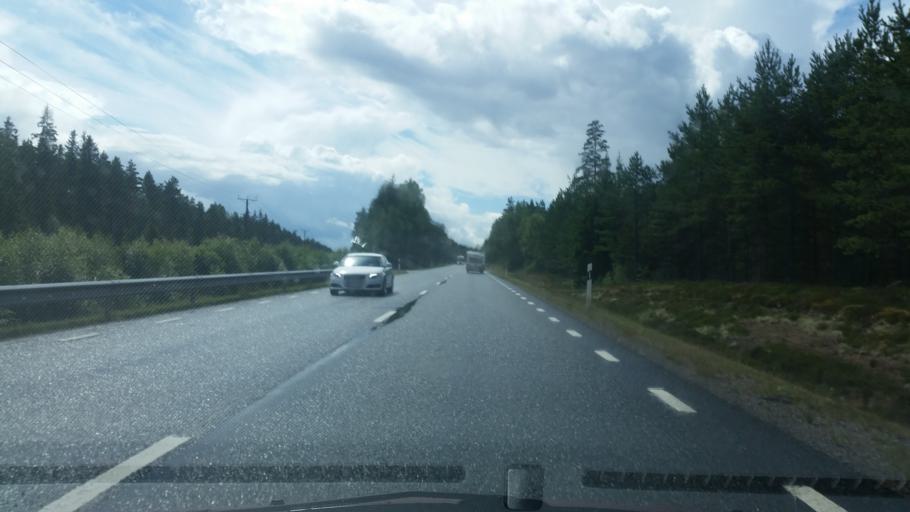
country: SE
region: Joenkoeping
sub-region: Gislaveds Kommun
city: Gislaved
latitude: 57.3951
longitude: 13.5919
